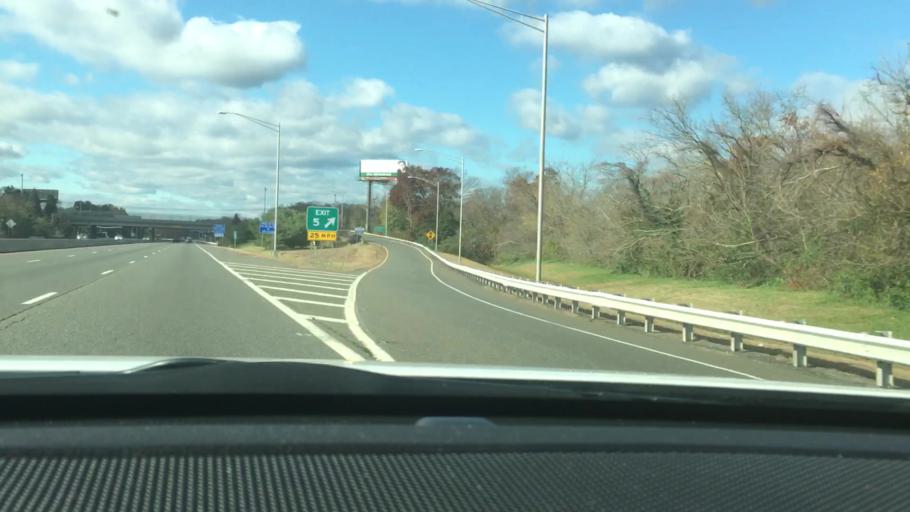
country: US
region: New Jersey
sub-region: Atlantic County
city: Pleasantville
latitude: 39.4007
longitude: -74.5212
